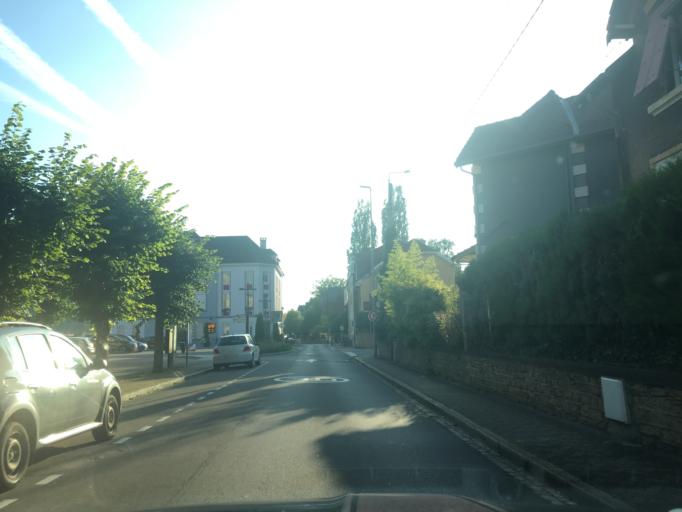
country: FR
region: Lorraine
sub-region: Departement de Meurthe-et-Moselle
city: Herserange
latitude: 49.5192
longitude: 5.7858
